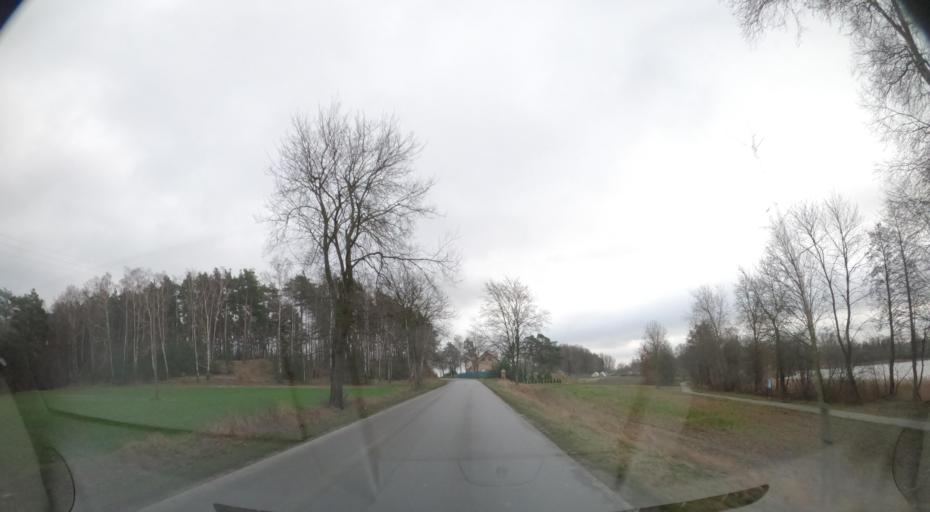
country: PL
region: Greater Poland Voivodeship
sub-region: Powiat pilski
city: Lobzenica
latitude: 53.2483
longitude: 17.2829
